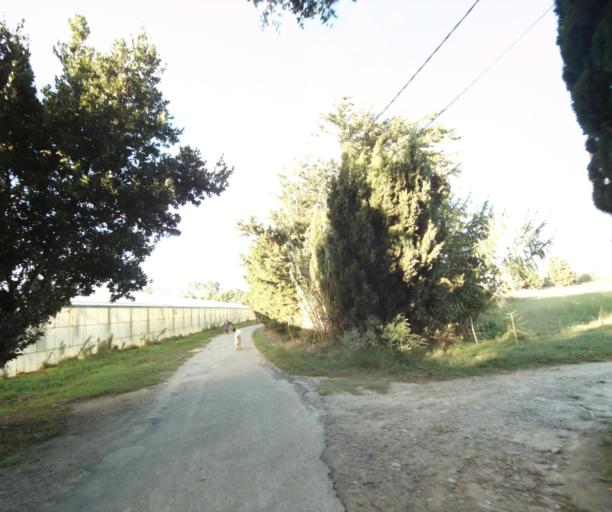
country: FR
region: Languedoc-Roussillon
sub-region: Departement des Pyrenees-Orientales
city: Latour-Bas-Elne
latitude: 42.5781
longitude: 3.0122
